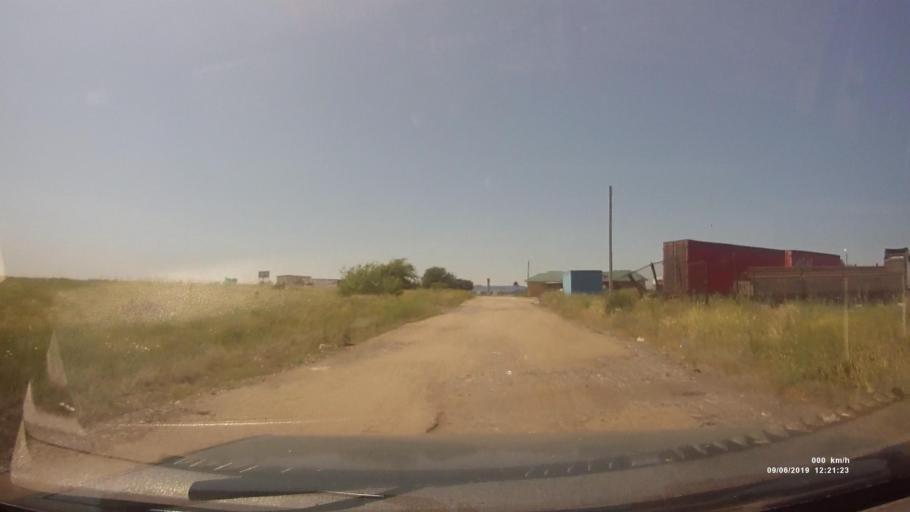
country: RU
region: Rostov
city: Kamensk-Shakhtinskiy
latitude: 48.2509
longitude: 40.2957
